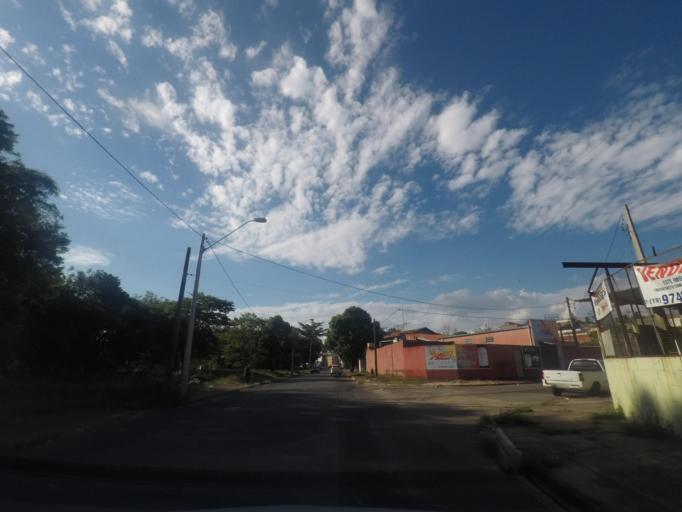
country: BR
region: Sao Paulo
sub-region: Sumare
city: Sumare
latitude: -22.8148
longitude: -47.2659
